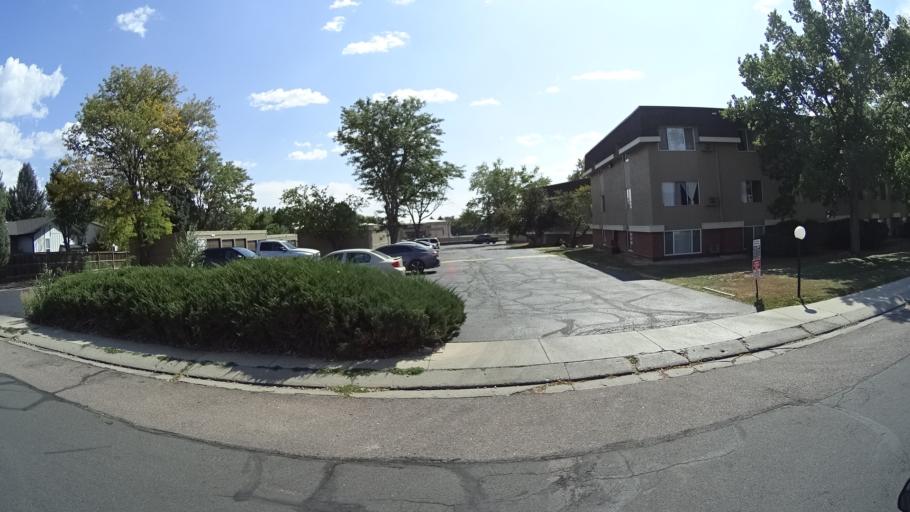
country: US
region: Colorado
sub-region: El Paso County
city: Cimarron Hills
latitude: 38.8705
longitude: -104.7541
